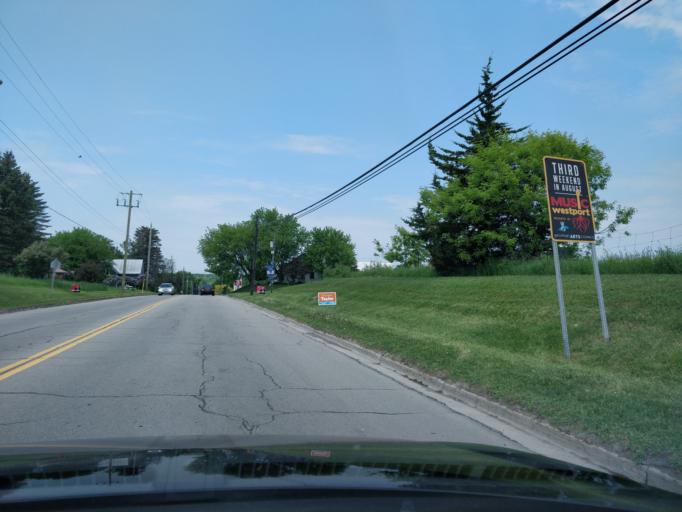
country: CA
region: Ontario
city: Perth
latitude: 44.6715
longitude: -76.3941
